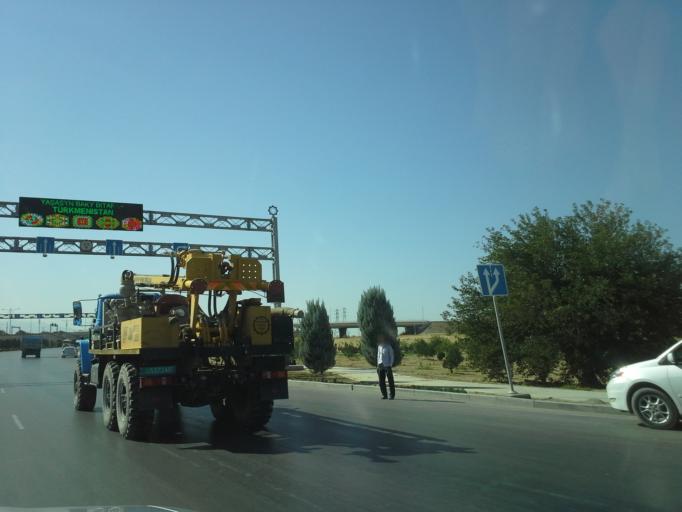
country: TM
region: Ahal
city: Annau
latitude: 37.9117
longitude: 58.4910
